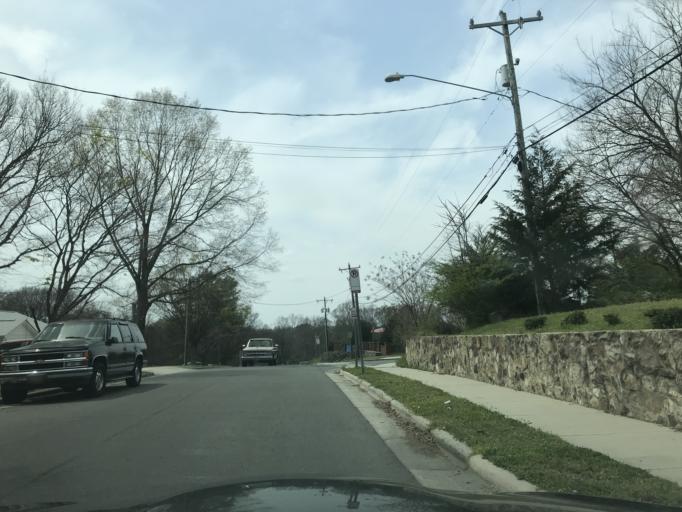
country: US
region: North Carolina
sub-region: Orange County
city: Chapel Hill
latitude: 35.9172
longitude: -79.0616
